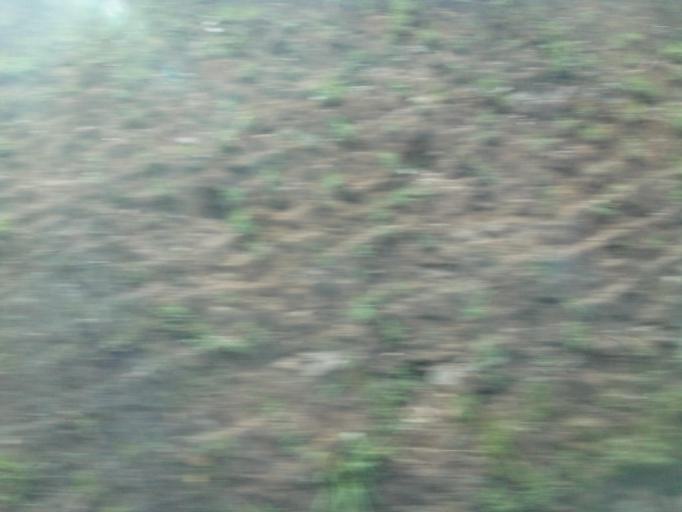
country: BR
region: Minas Gerais
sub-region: Santa Luzia
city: Santa Luzia
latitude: -19.8701
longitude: -43.8422
